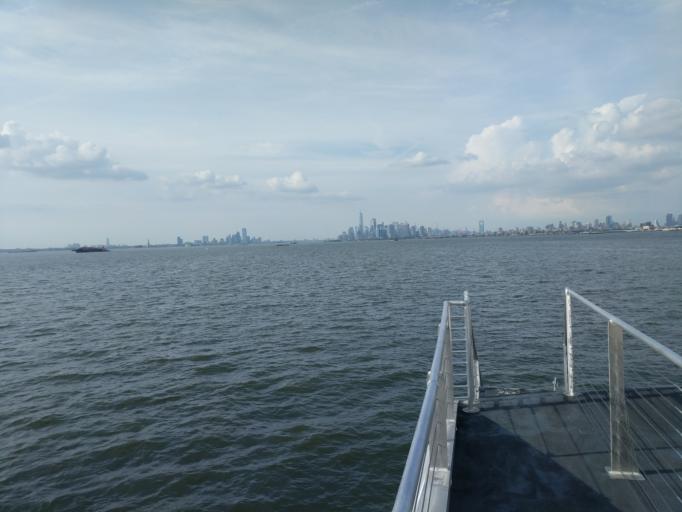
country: US
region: New York
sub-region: Kings County
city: Bensonhurst
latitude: 40.6464
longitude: -74.0350
